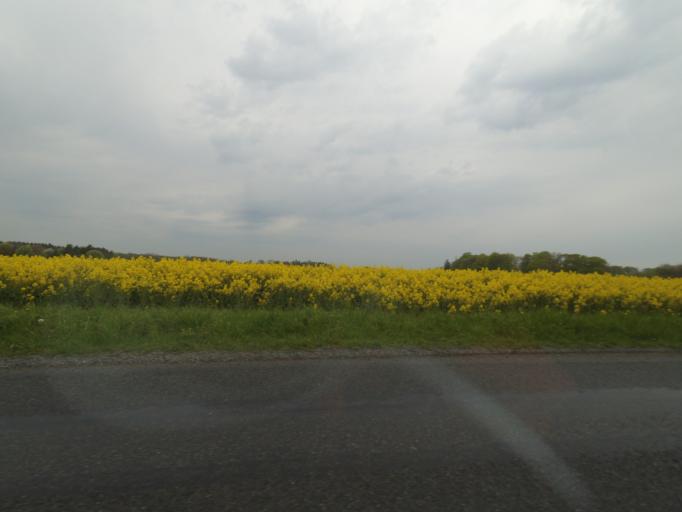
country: DK
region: South Denmark
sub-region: Svendborg Kommune
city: Svendborg
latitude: 55.1688
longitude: 10.6282
